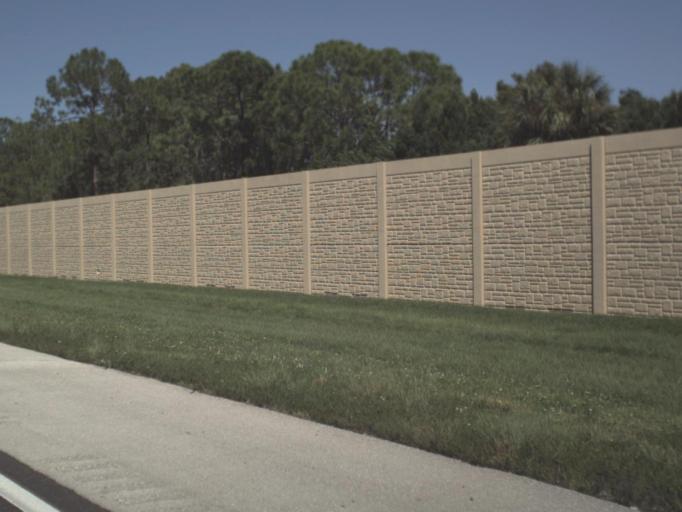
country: US
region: Florida
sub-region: Lee County
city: Bonita Springs
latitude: 26.3182
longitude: -81.7466
